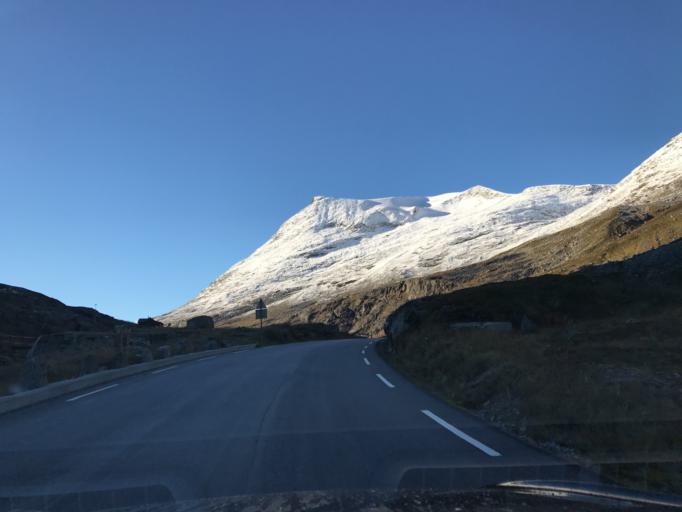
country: NO
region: More og Romsdal
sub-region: Rauma
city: Andalsnes
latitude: 62.4553
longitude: 7.6668
